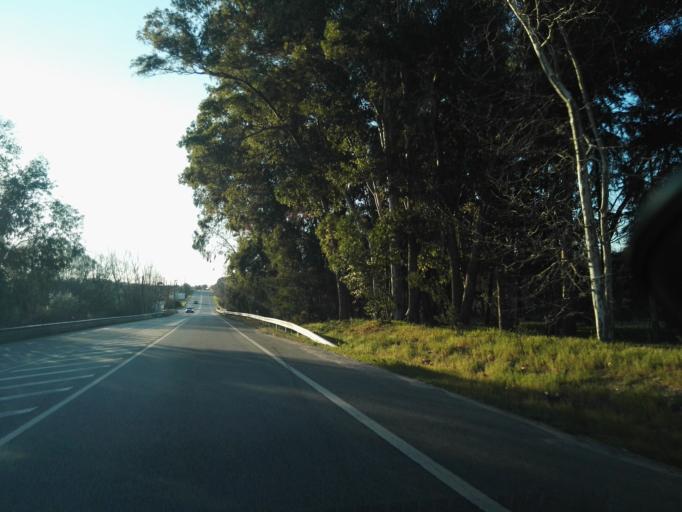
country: PT
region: Evora
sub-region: Montemor-O-Novo
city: Montemor-o-Novo
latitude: 38.6447
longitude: -8.1906
